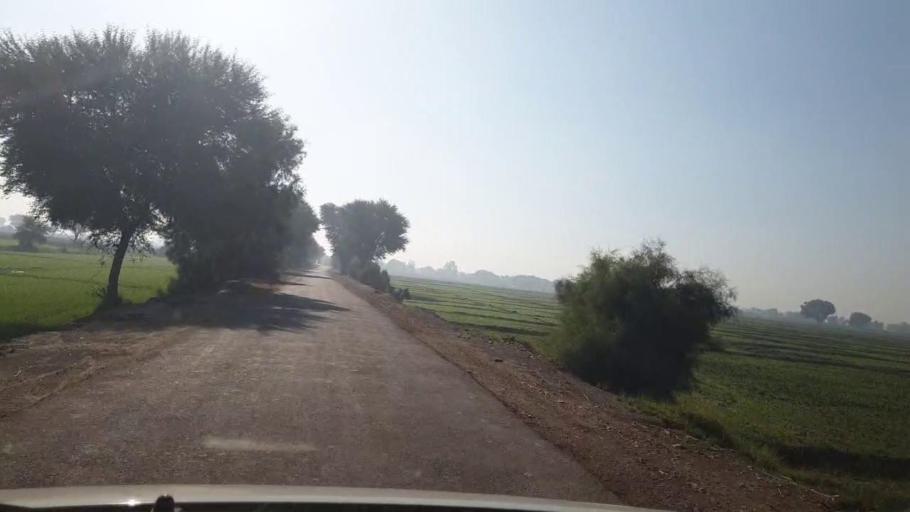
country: PK
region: Sindh
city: Dadu
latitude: 26.6626
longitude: 67.8187
